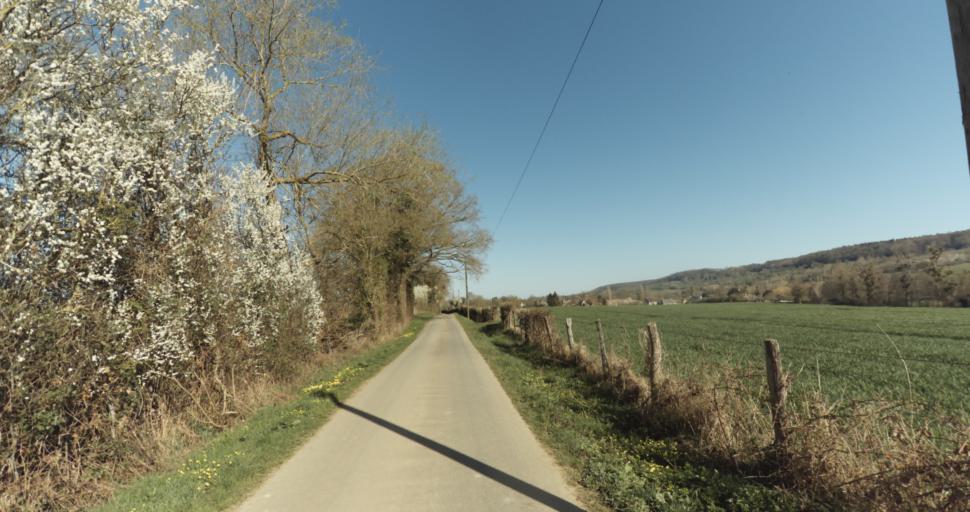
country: FR
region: Lower Normandy
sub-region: Departement du Calvados
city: Saint-Pierre-sur-Dives
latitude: 48.9709
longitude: 0.0372
